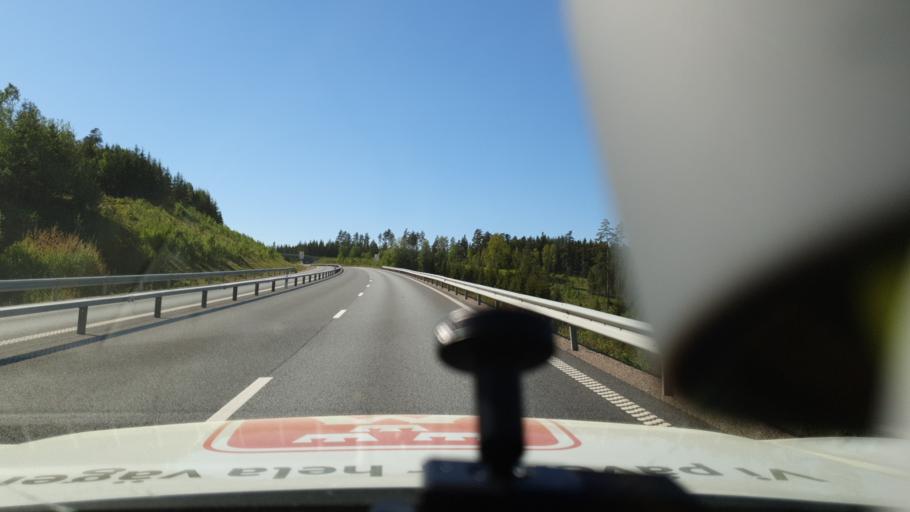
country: SE
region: Joenkoeping
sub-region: Vetlanda Kommun
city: Vetlanda
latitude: 57.4198
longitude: 15.2016
